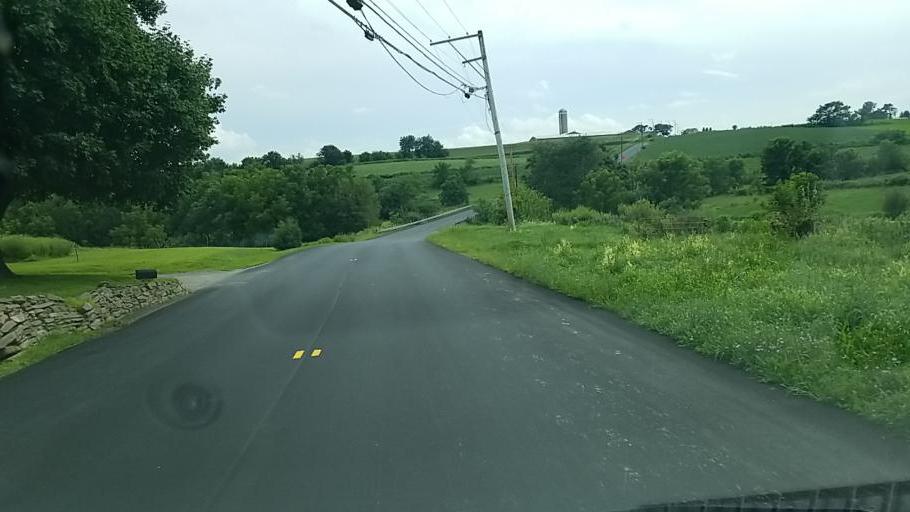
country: US
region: Pennsylvania
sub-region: Dauphin County
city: Elizabethville
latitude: 40.5933
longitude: -76.8099
